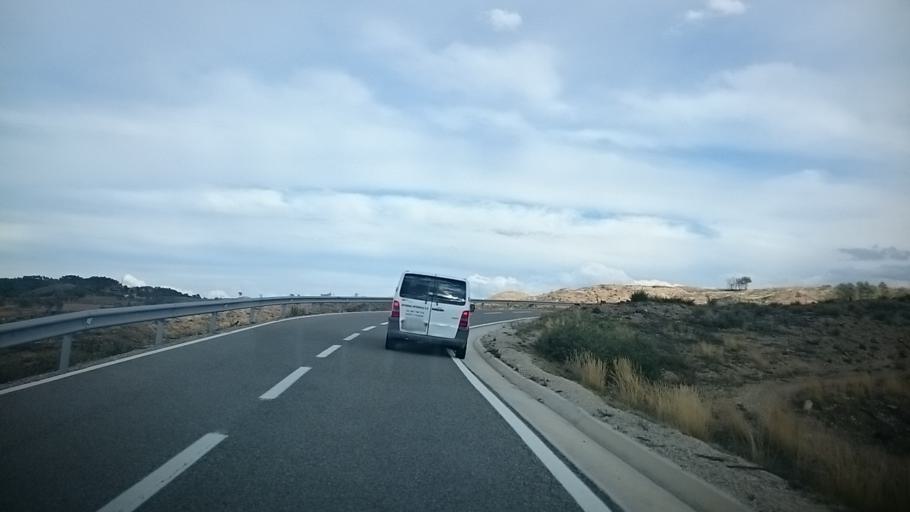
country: ES
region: Catalonia
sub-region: Provincia de Barcelona
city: Castelloli
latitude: 41.6268
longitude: 1.6773
